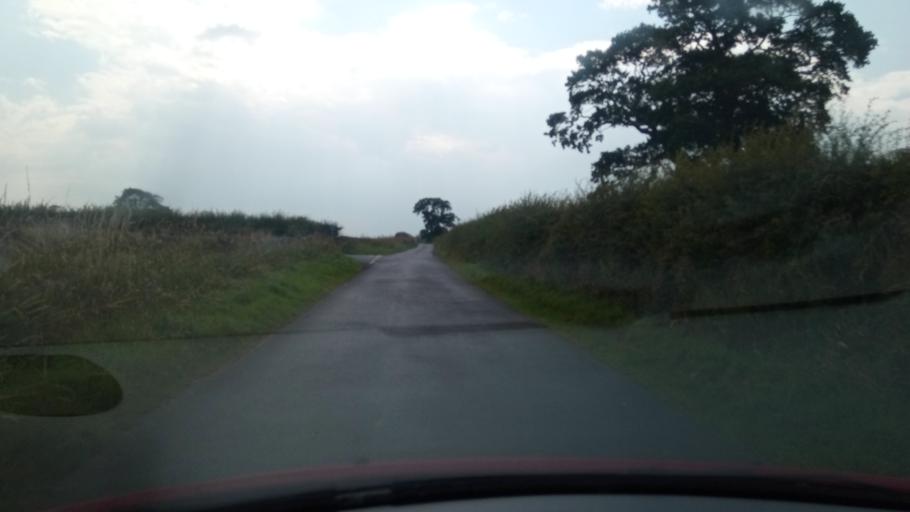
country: GB
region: Scotland
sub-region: The Scottish Borders
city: Kelso
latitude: 55.5761
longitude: -2.4761
